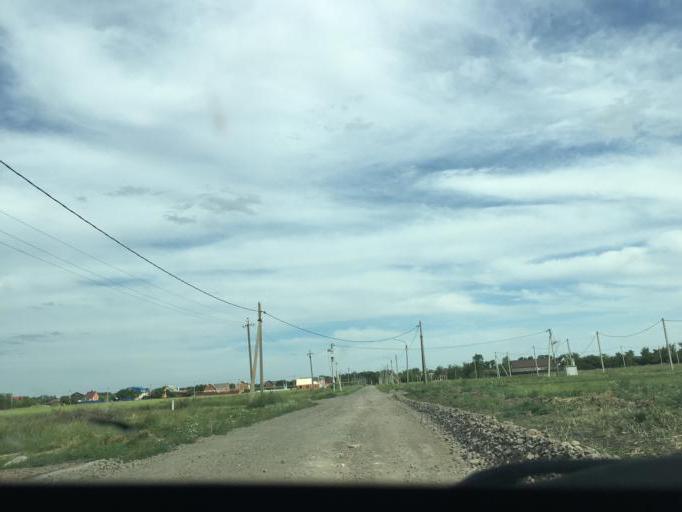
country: RU
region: Krasnodarskiy
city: Kushchevskaya
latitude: 46.5536
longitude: 39.6675
